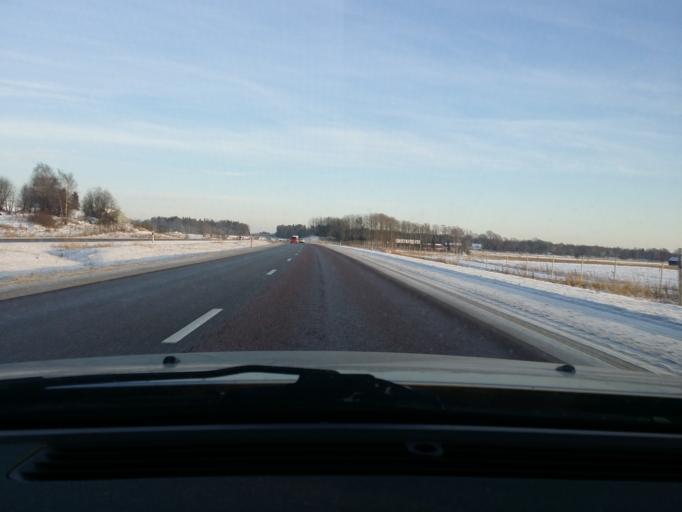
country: SE
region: OErebro
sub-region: Lindesbergs Kommun
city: Frovi
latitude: 59.3065
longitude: 15.3710
